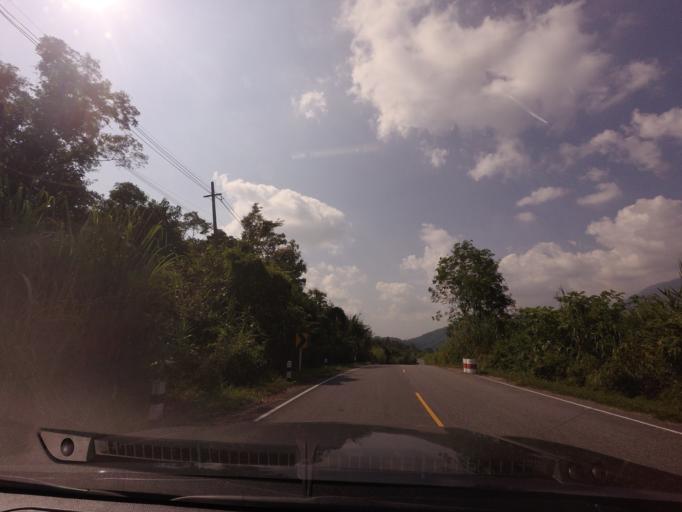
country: TH
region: Nan
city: Santi Suk
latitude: 18.9729
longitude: 101.0210
